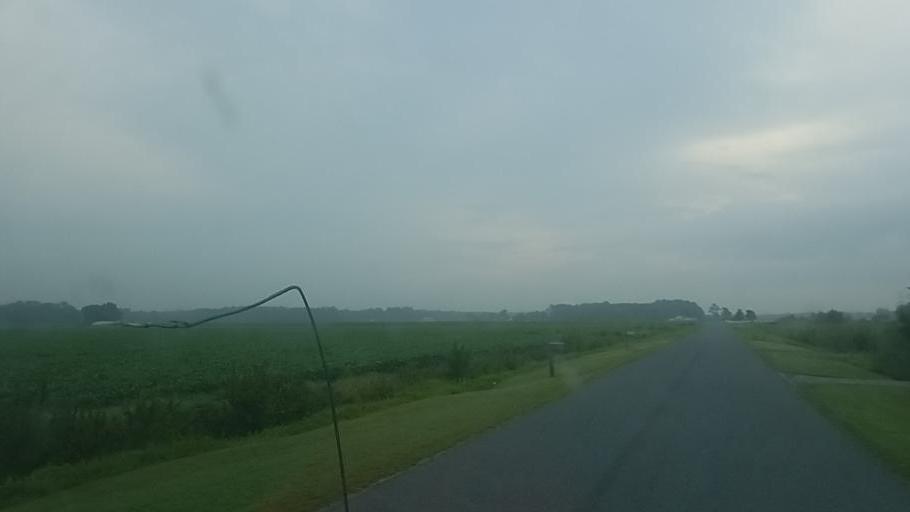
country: US
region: Maryland
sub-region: Wicomico County
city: Pittsville
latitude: 38.4521
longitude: -75.3657
